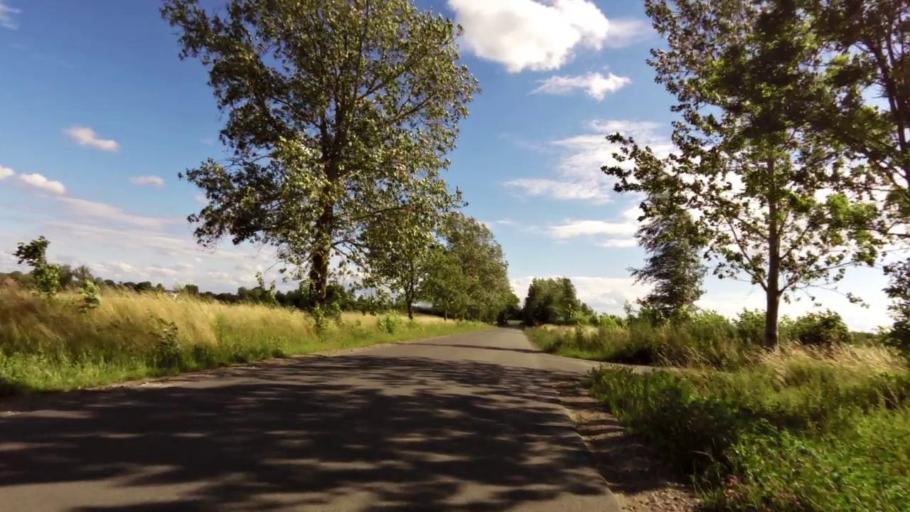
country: PL
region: West Pomeranian Voivodeship
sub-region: Powiat slawienski
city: Slawno
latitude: 54.4402
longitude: 16.7337
